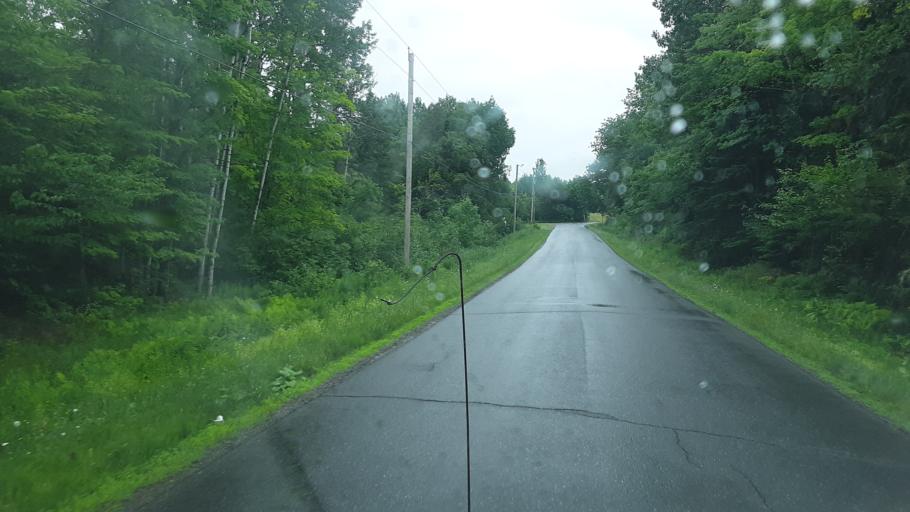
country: US
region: Maine
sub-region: Aroostook County
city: Presque Isle
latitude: 46.6830
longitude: -68.2162
